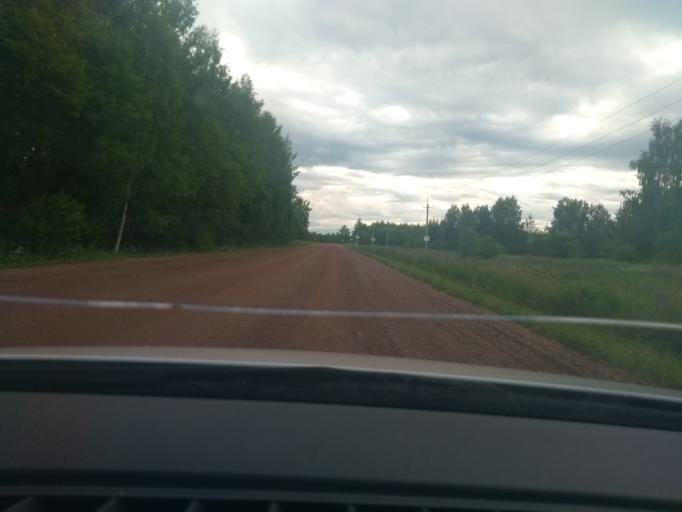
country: RU
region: Perm
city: Sylva
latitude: 57.8173
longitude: 56.7252
